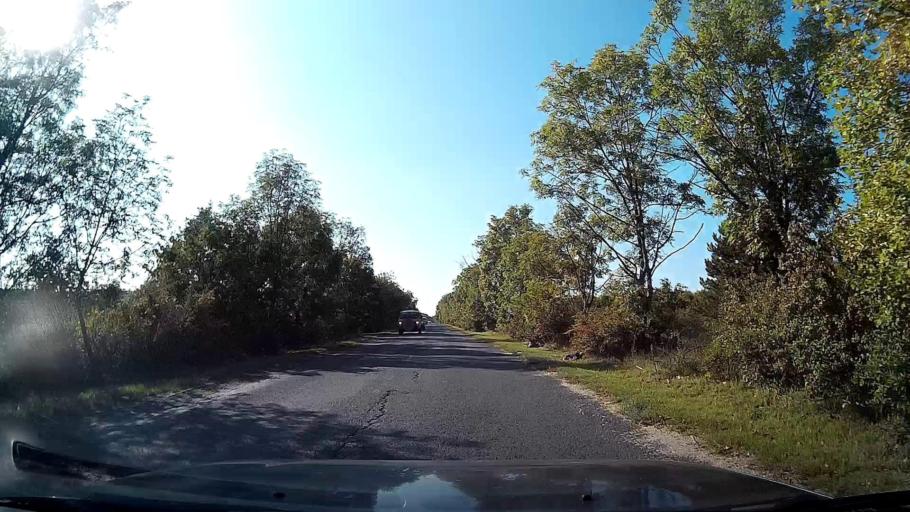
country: HU
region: Pest
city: Diosd
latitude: 47.4210
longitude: 18.9796
